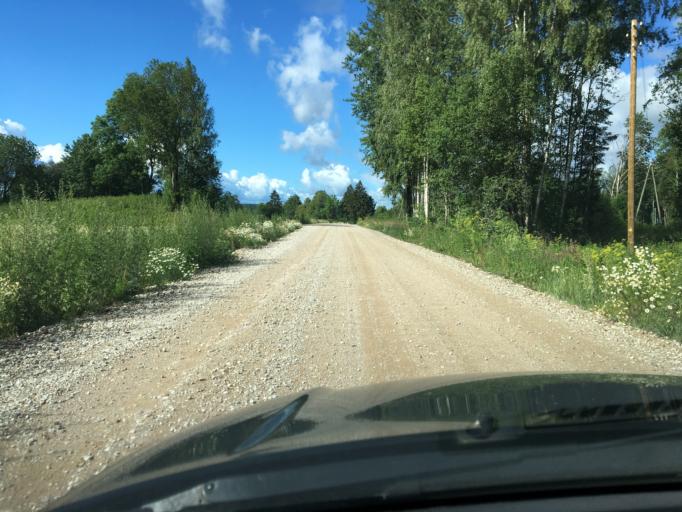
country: LV
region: Kuldigas Rajons
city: Kuldiga
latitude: 56.8404
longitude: 21.9259
